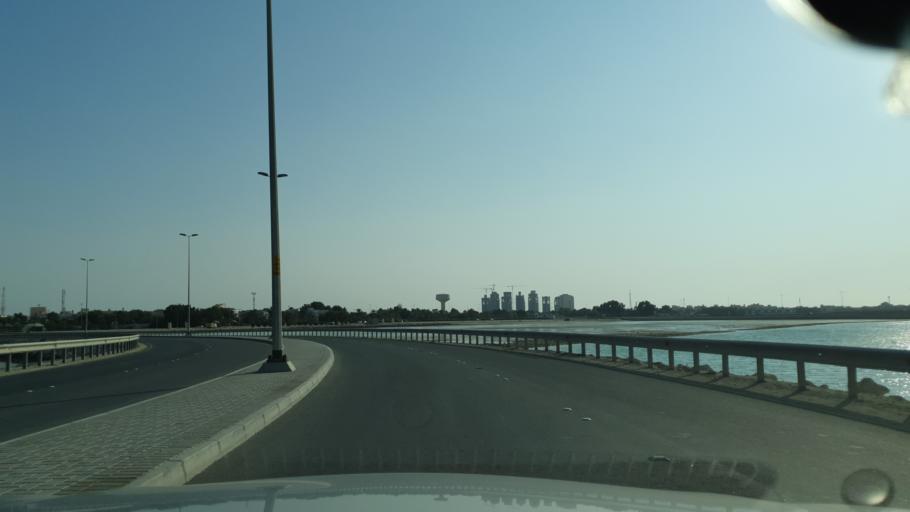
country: BH
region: Manama
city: Jidd Hafs
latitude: 26.2275
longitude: 50.4572
